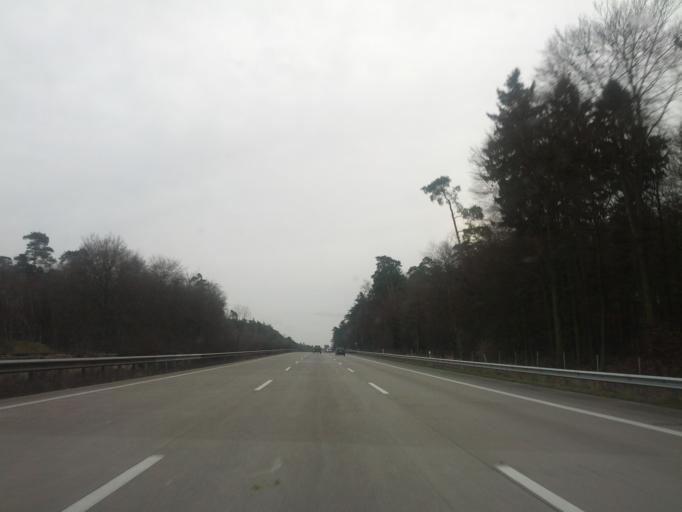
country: DE
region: Lower Saxony
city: Brackel
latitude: 53.3200
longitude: 10.0593
